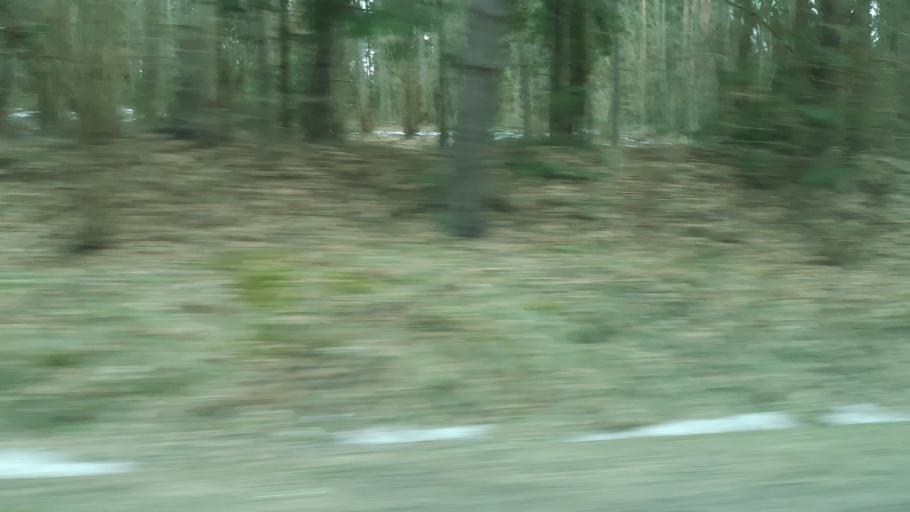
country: PL
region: Podlasie
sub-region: Suwalki
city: Suwalki
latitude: 54.2904
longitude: 22.9553
